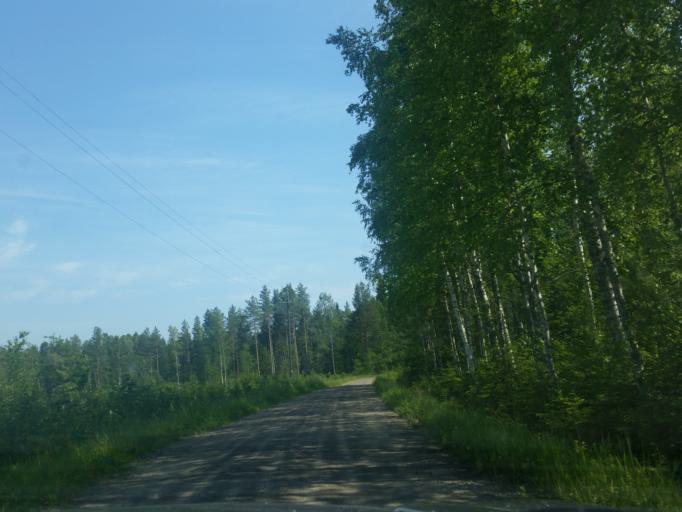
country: FI
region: Northern Savo
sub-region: Ylae-Savo
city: Keitele
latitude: 63.0979
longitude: 26.5680
